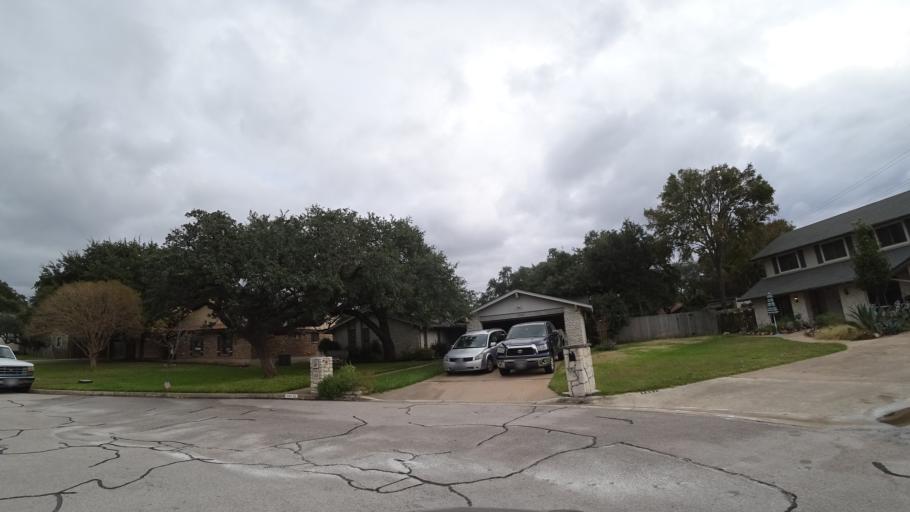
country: US
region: Texas
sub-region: Williamson County
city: Round Rock
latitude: 30.4970
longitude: -97.6976
